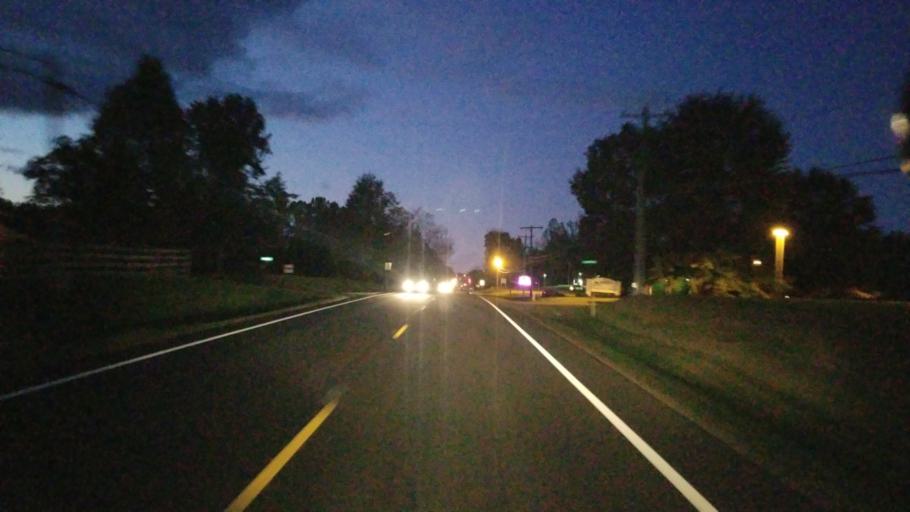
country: US
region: Ohio
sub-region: Vinton County
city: McArthur
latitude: 39.2624
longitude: -82.4765
